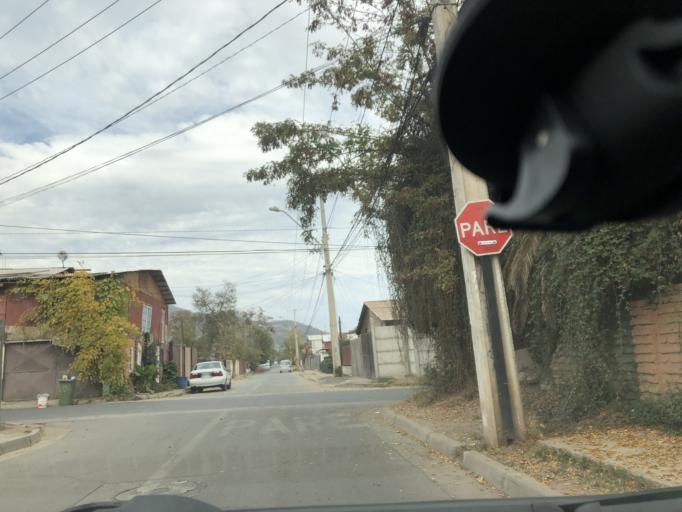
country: CL
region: Santiago Metropolitan
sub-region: Provincia de Cordillera
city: Puente Alto
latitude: -33.6099
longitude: -70.5321
